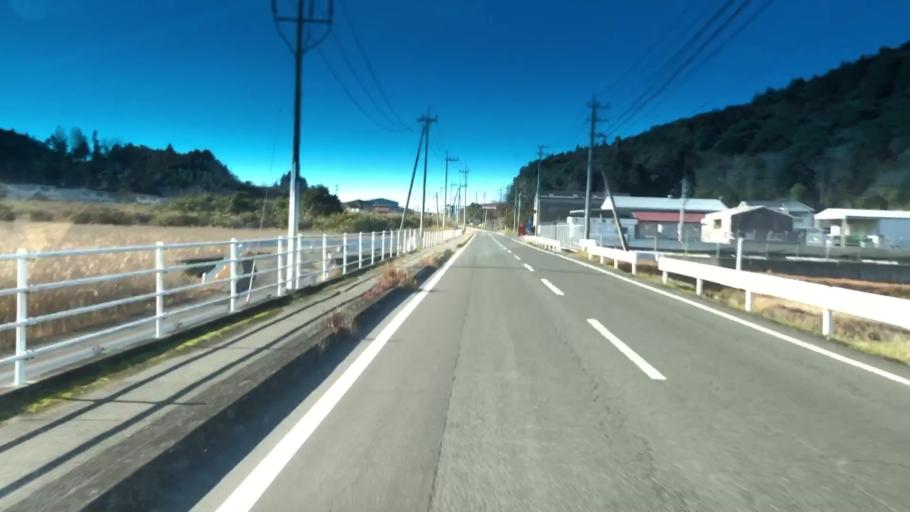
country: JP
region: Kagoshima
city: Satsumasendai
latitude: 31.8186
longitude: 130.2673
